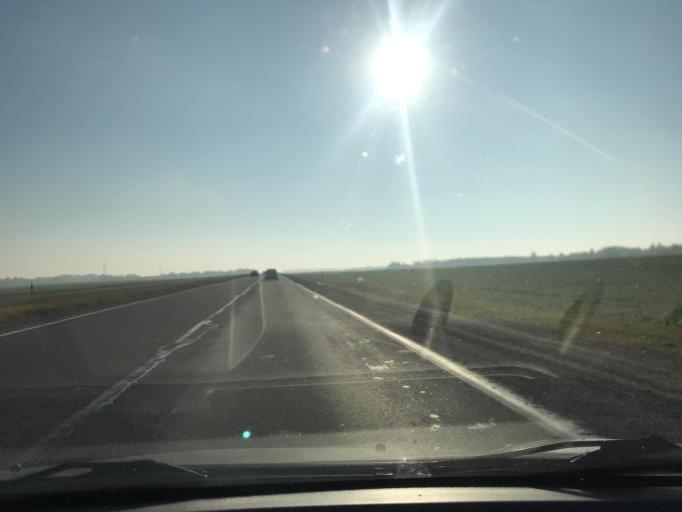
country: BY
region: Minsk
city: Dukora
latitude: 53.6518
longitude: 27.9691
